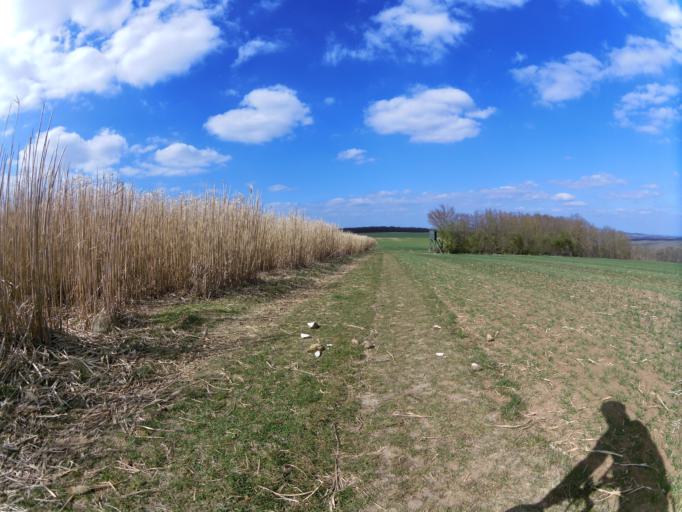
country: DE
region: Bavaria
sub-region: Regierungsbezirk Unterfranken
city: Dettelbach
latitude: 49.8314
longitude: 10.1695
